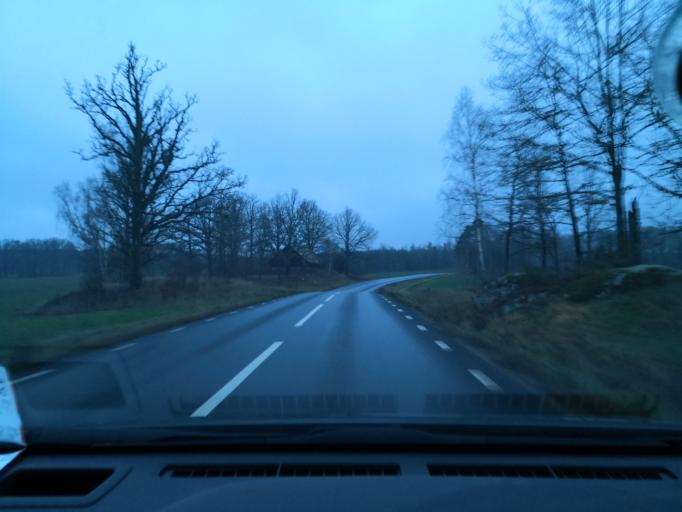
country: SE
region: Soedermanland
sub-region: Eskilstuna Kommun
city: Skogstorp
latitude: 59.2291
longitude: 16.3167
